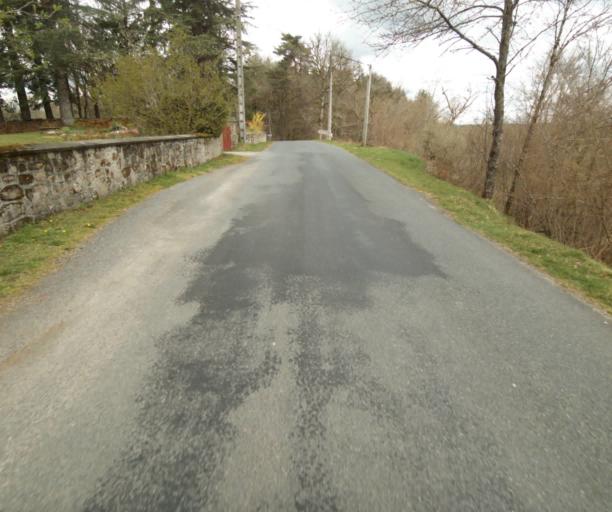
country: FR
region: Limousin
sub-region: Departement de la Correze
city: Correze
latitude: 45.3313
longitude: 1.9530
